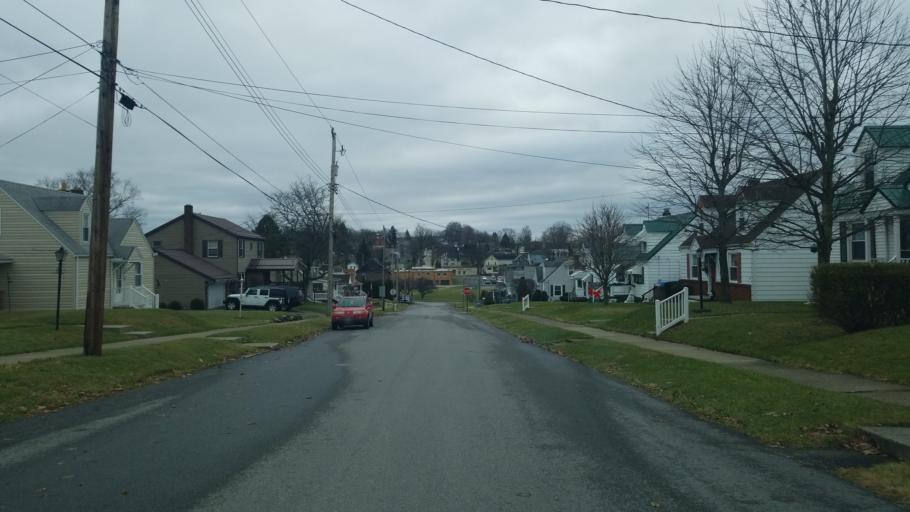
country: US
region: Pennsylvania
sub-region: Clearfield County
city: DuBois
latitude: 41.1309
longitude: -78.7616
